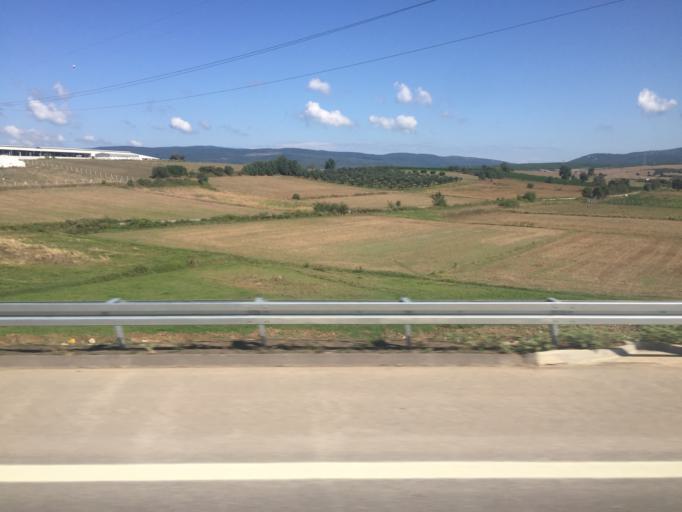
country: TR
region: Bursa
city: Karacabey
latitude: 40.2534
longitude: 28.4603
